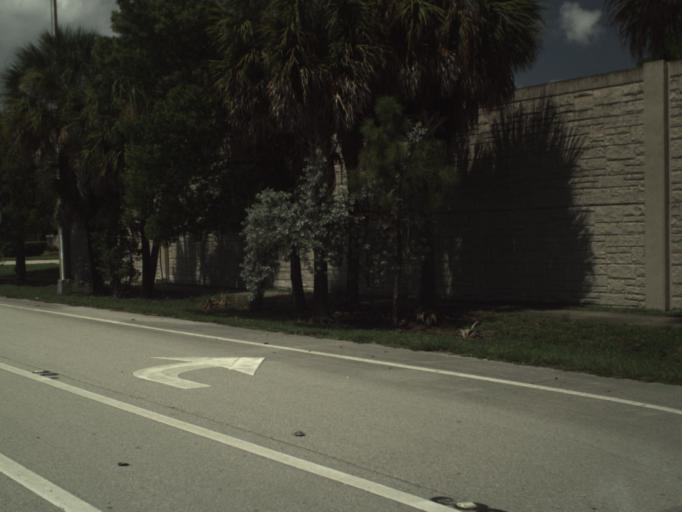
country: US
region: Florida
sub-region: Palm Beach County
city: Kings Point
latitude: 26.4010
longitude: -80.2037
